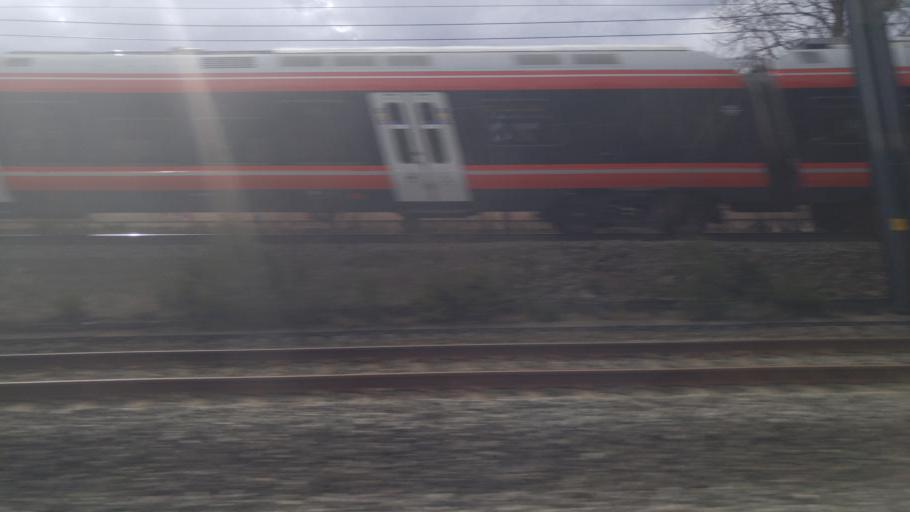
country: NO
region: Akershus
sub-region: Ullensaker
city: Klofta
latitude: 60.0693
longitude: 11.1395
